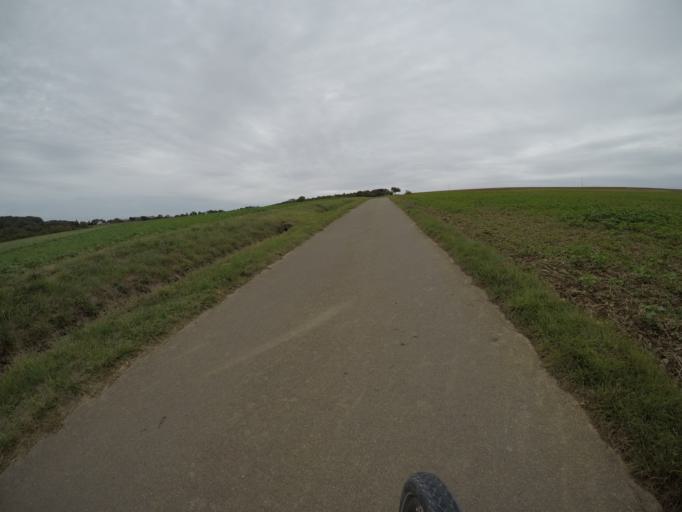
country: DE
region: Baden-Wuerttemberg
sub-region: Regierungsbezirk Stuttgart
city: Eberdingen
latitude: 48.8910
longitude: 8.9754
